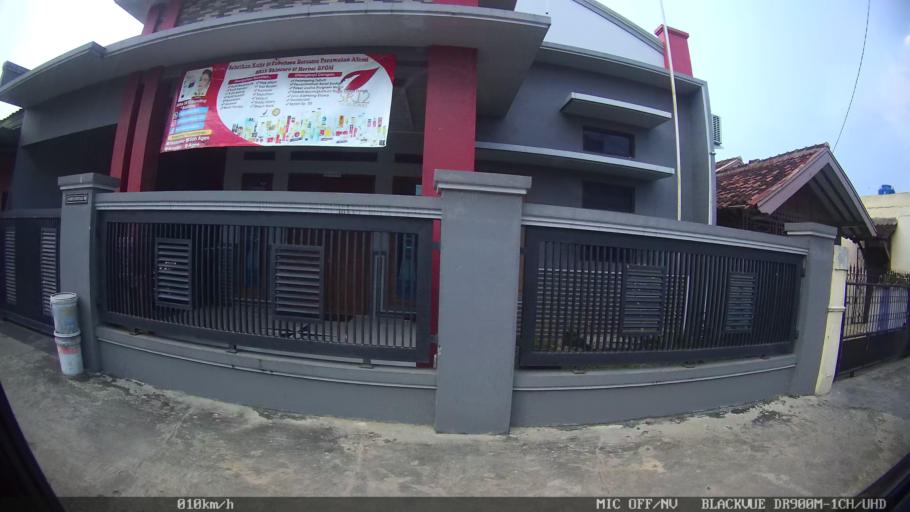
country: ID
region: Lampung
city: Kedaton
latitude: -5.3949
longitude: 105.2074
